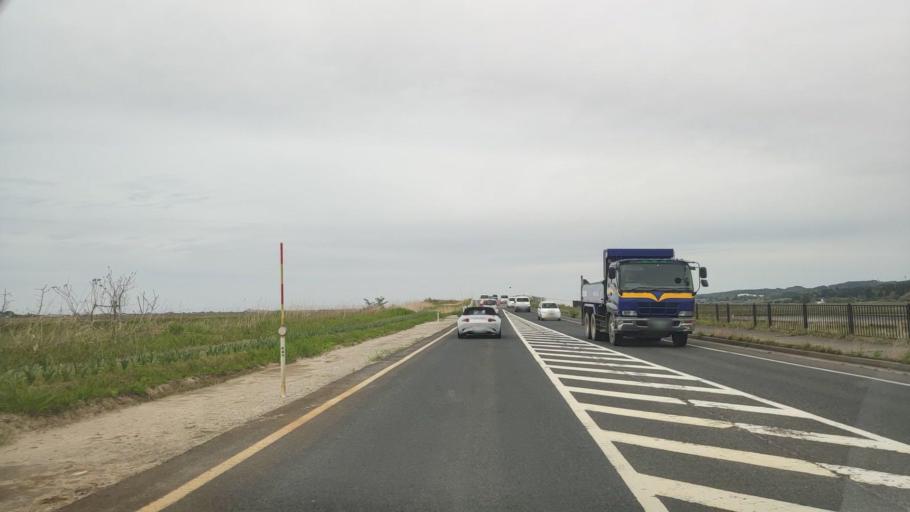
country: JP
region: Niigata
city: Niitsu-honcho
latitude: 37.7569
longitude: 139.0920
